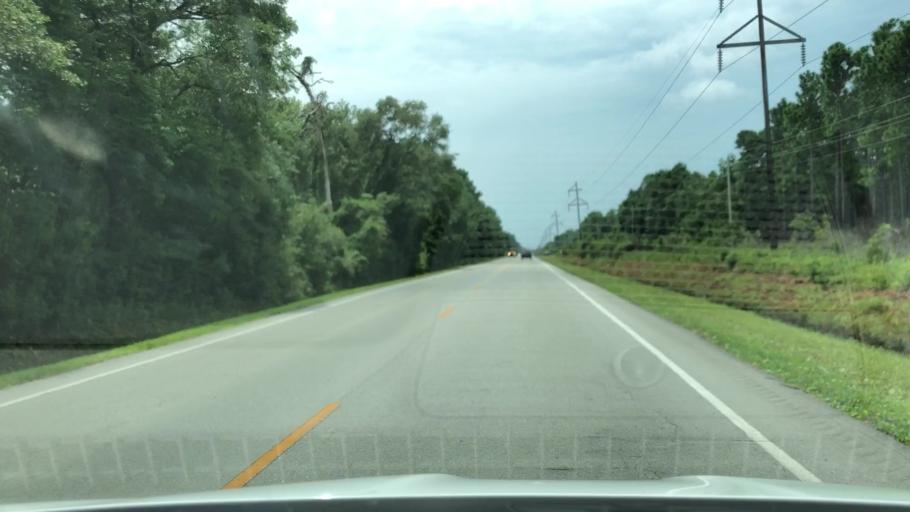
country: US
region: North Carolina
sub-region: Carteret County
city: Newport
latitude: 34.7577
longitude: -76.8733
